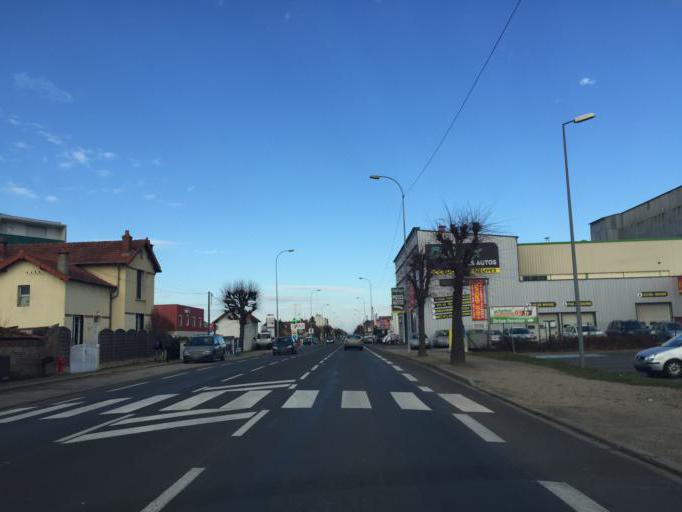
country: FR
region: Auvergne
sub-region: Departement de l'Allier
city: Moulins
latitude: 46.5470
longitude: 3.3408
